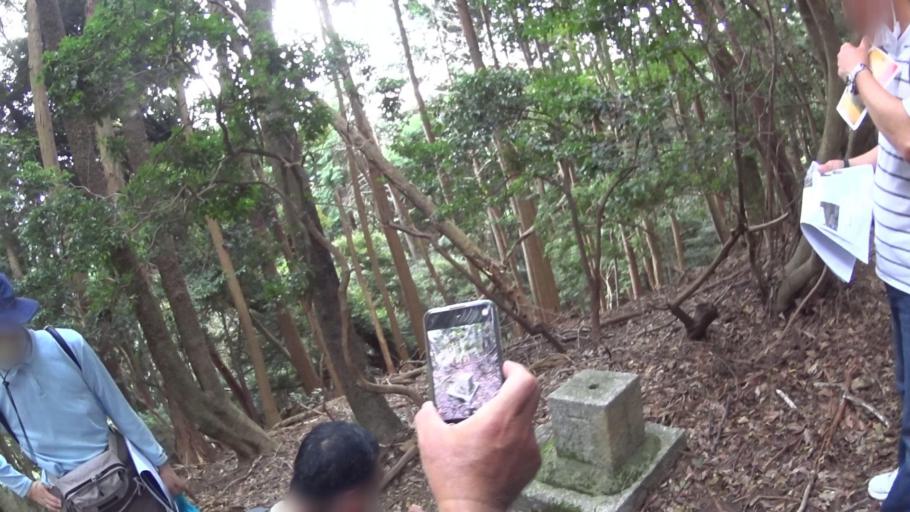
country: JP
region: Osaka
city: Kishiwada
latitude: 34.4929
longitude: 135.3256
